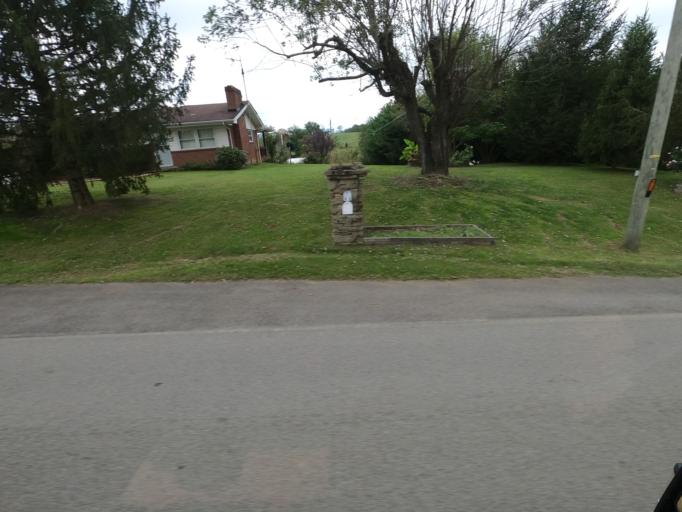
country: US
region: Tennessee
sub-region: Washington County
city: Jonesborough
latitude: 36.2232
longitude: -82.5830
